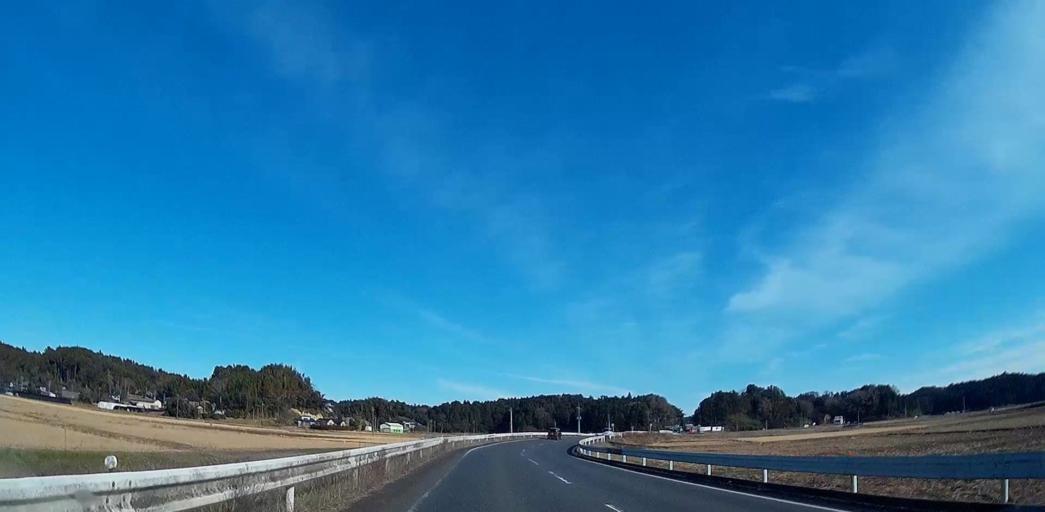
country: JP
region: Chiba
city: Yokaichiba
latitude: 35.7346
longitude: 140.5332
